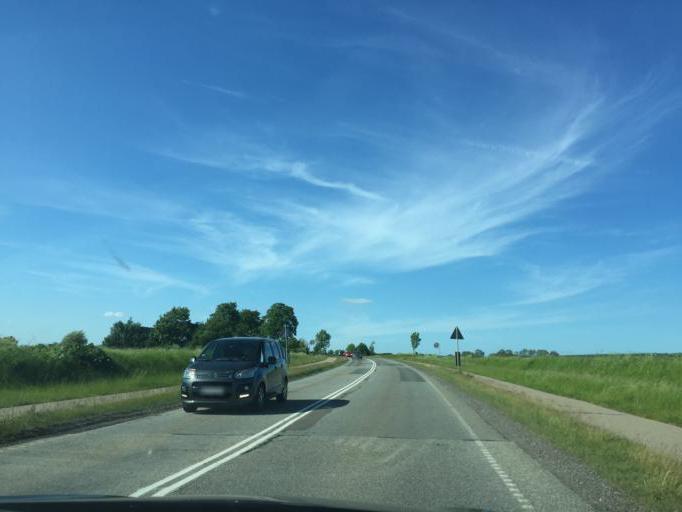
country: DK
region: Zealand
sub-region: Stevns Kommune
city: Harlev
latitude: 55.3560
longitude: 12.2493
